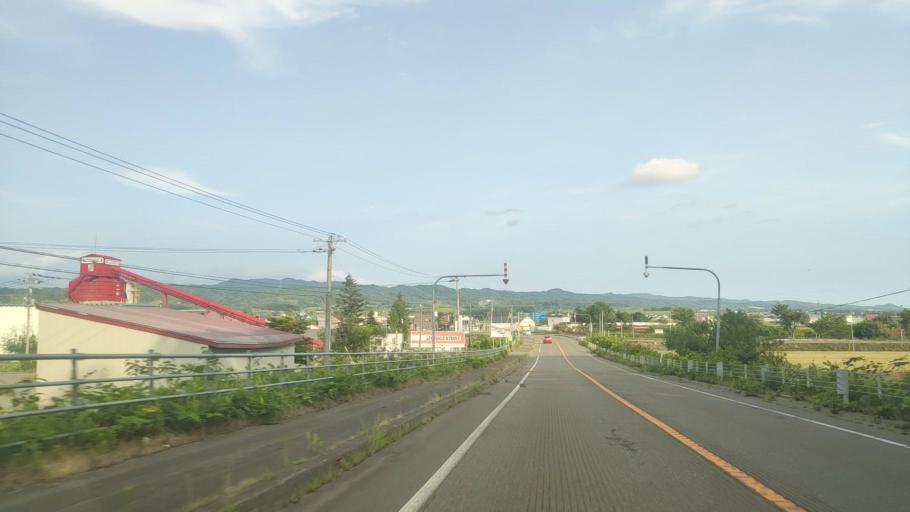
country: JP
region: Hokkaido
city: Iwamizawa
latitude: 43.0216
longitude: 141.8514
